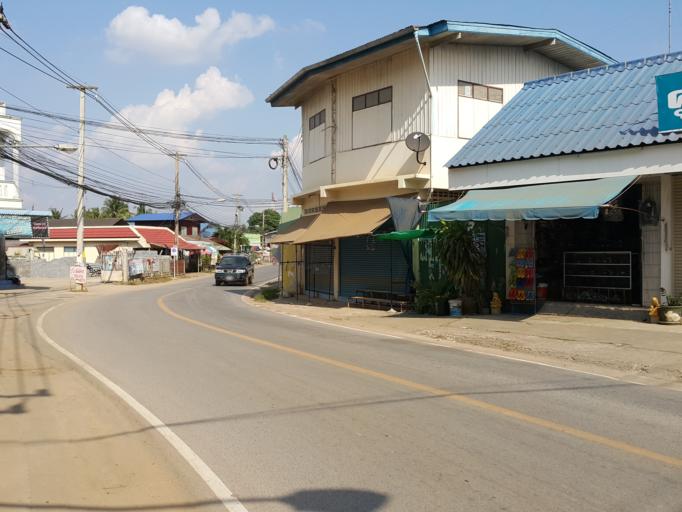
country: TH
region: Sukhothai
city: Thung Saliam
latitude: 17.3177
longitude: 99.5545
